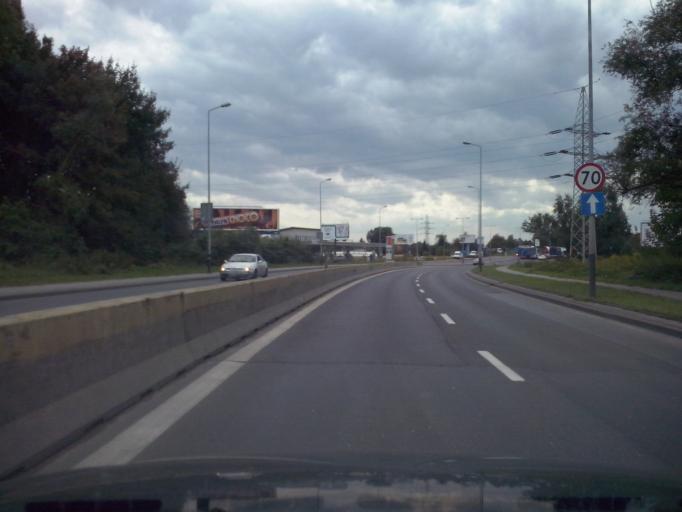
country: PL
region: Lesser Poland Voivodeship
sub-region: Krakow
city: Krakow
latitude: 50.0592
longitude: 20.0031
